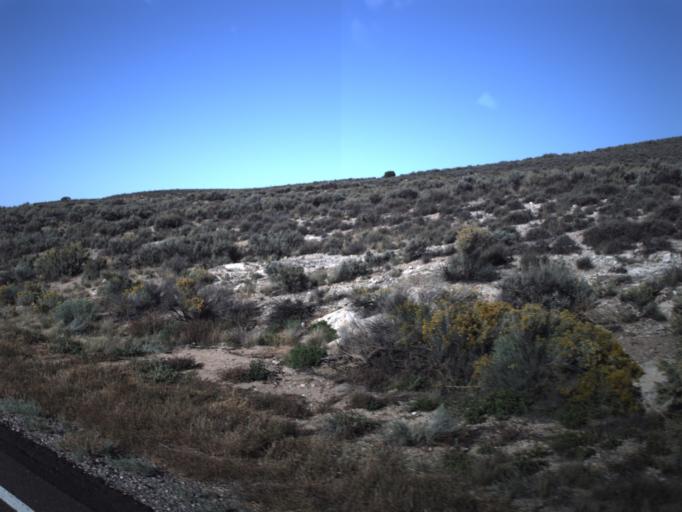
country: US
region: Utah
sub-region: Washington County
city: Enterprise
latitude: 37.7523
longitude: -113.9987
